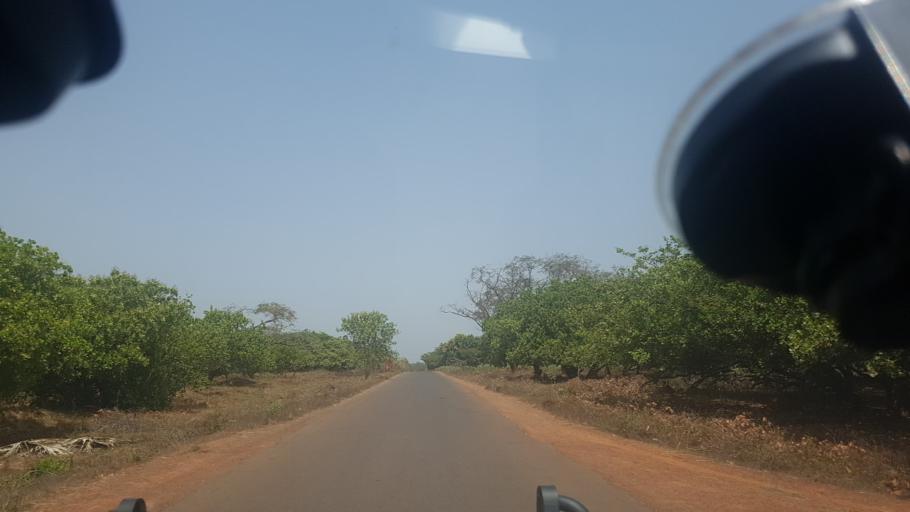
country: GW
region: Oio
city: Bissora
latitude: 12.3031
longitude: -15.7636
